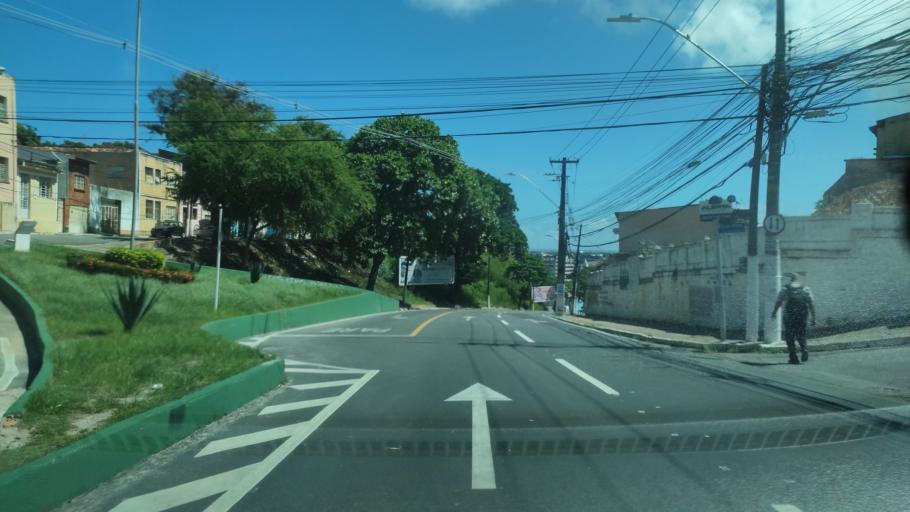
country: BR
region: Alagoas
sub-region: Maceio
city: Maceio
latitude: -9.6589
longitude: -35.7364
